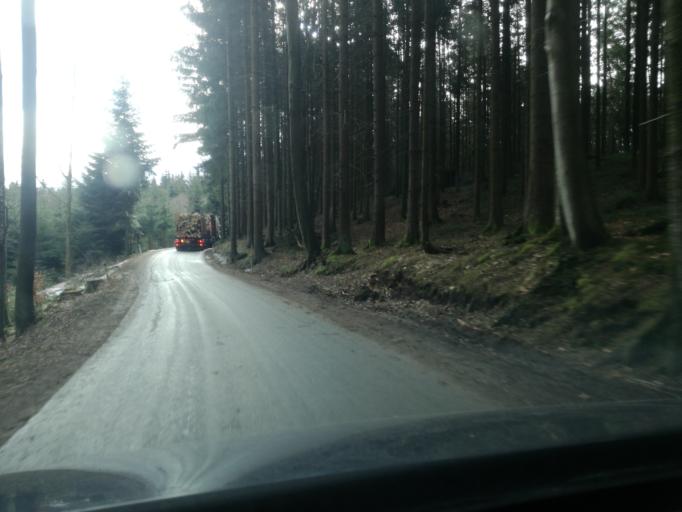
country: AT
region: Upper Austria
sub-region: Politischer Bezirk Ried im Innkreis
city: Waldzell
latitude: 48.1083
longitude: 13.4490
